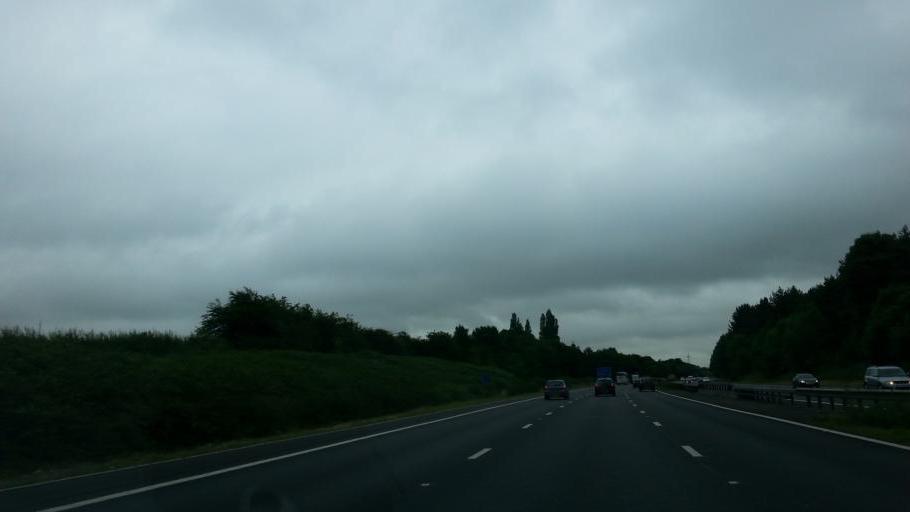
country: GB
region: England
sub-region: Leicestershire
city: Cosby
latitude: 52.5258
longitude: -1.1753
